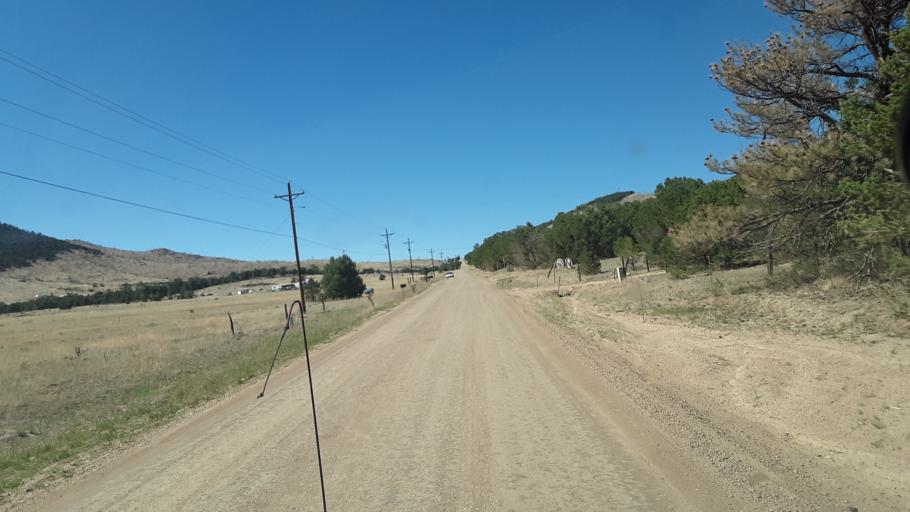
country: US
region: Colorado
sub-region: Custer County
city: Westcliffe
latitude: 38.3127
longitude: -105.4866
